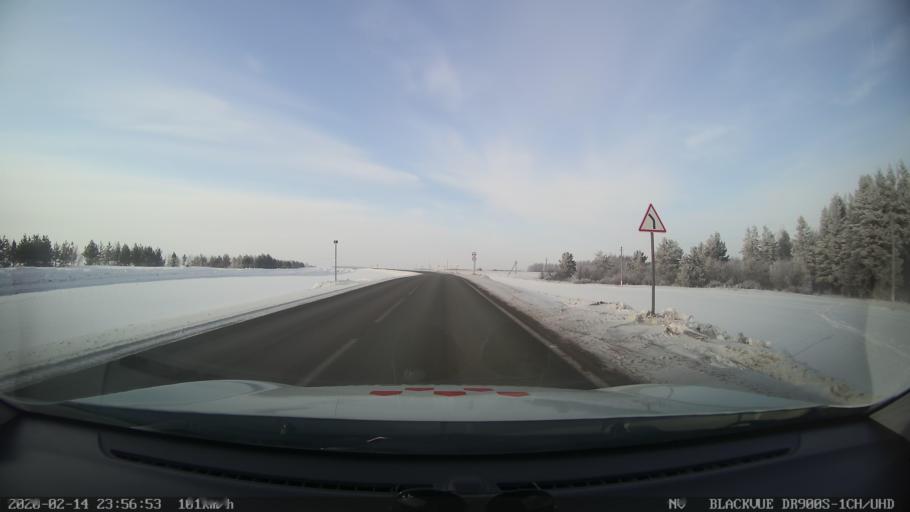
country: RU
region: Tatarstan
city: Kuybyshevskiy Zaton
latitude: 55.3294
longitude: 49.1223
